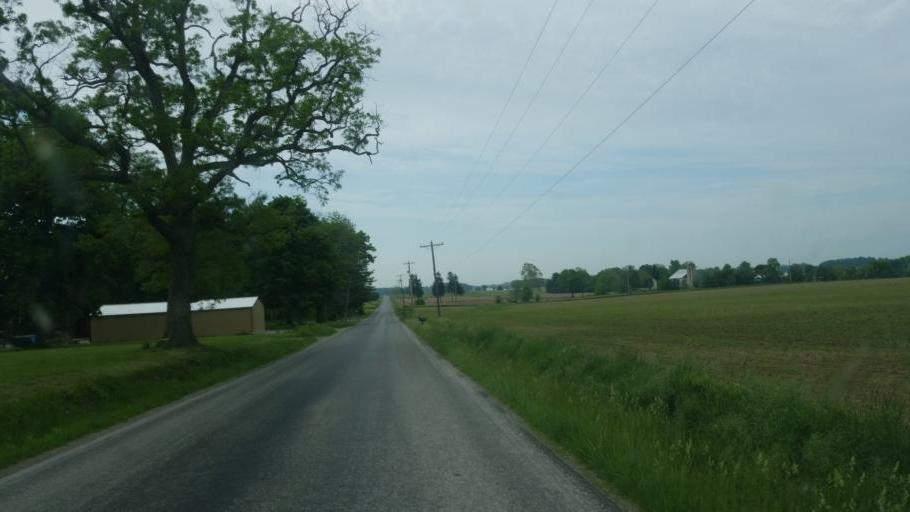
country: US
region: Ohio
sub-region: Wayne County
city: Dalton
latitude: 40.7658
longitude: -81.7550
